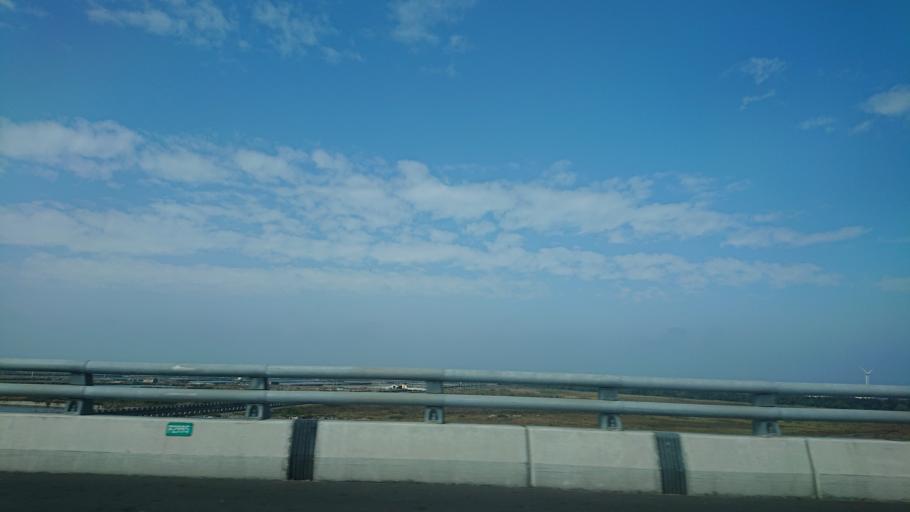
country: TW
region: Taiwan
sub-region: Changhua
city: Chang-hua
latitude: 23.9625
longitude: 120.3366
